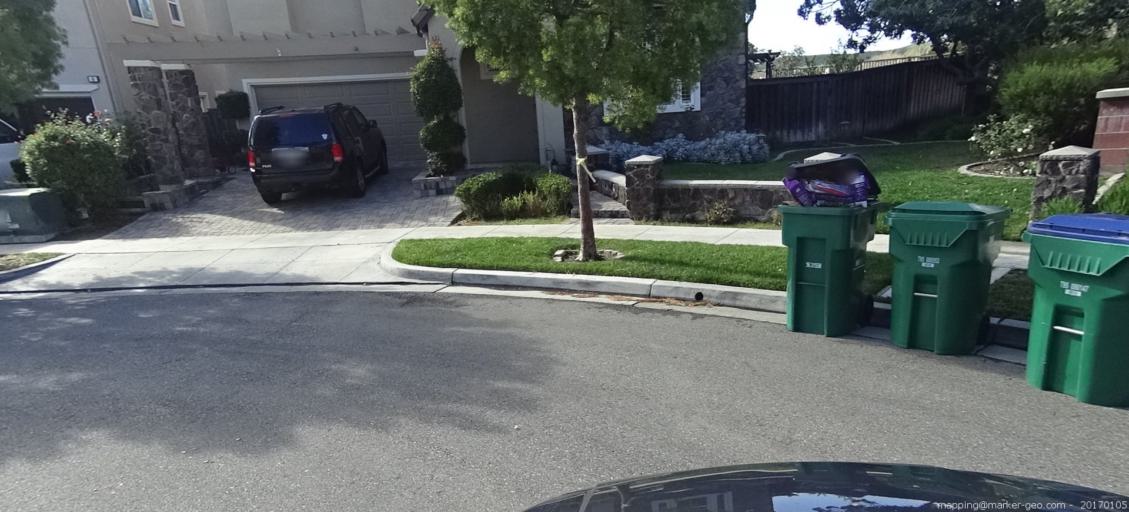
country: US
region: California
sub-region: Orange County
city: Ladera Ranch
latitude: 33.5470
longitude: -117.6368
